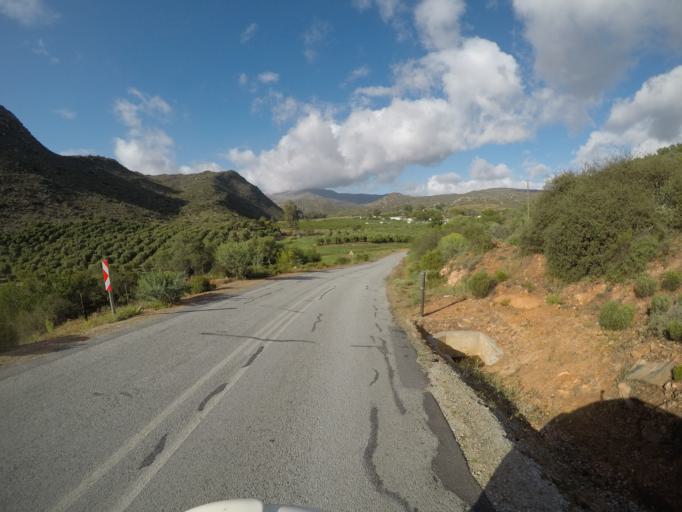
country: ZA
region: Western Cape
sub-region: West Coast District Municipality
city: Clanwilliam
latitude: -32.4365
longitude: 18.9458
